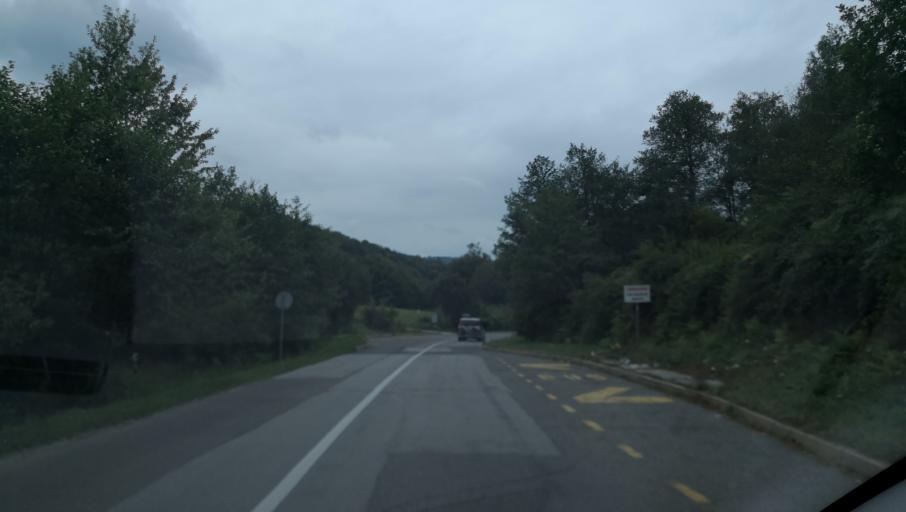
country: HR
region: Karlovacka
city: Ozalj
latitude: 45.5231
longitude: 15.3912
